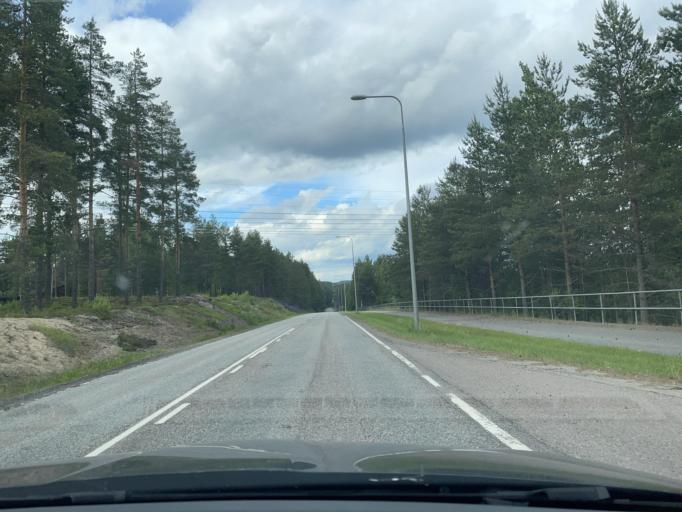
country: FI
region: Central Finland
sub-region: Jaemsae
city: Jaemsaenkoski
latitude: 61.9146
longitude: 25.1456
